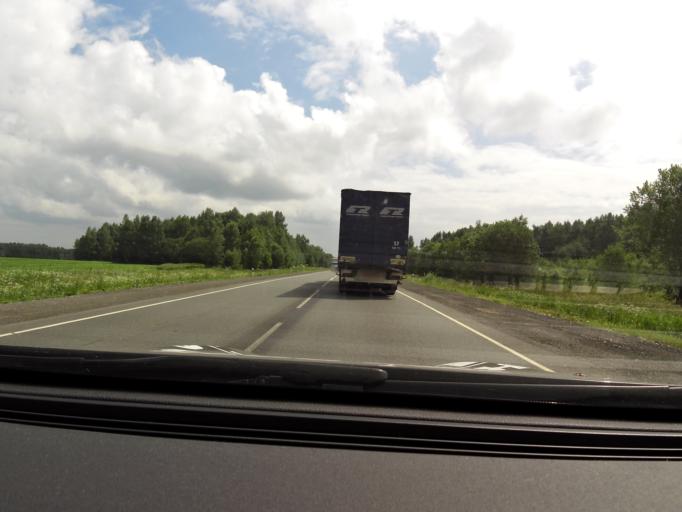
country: RU
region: Perm
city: Ust'-Kishert'
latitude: 57.1686
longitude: 57.1483
